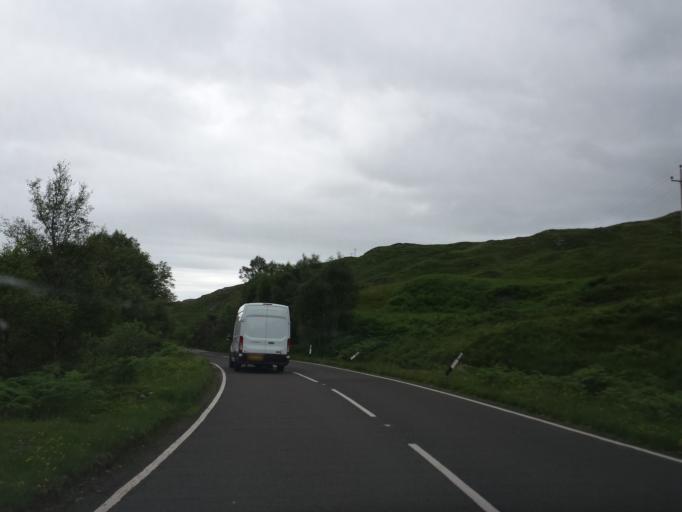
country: GB
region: Scotland
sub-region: Argyll and Bute
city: Isle Of Mull
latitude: 56.8851
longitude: -5.6200
